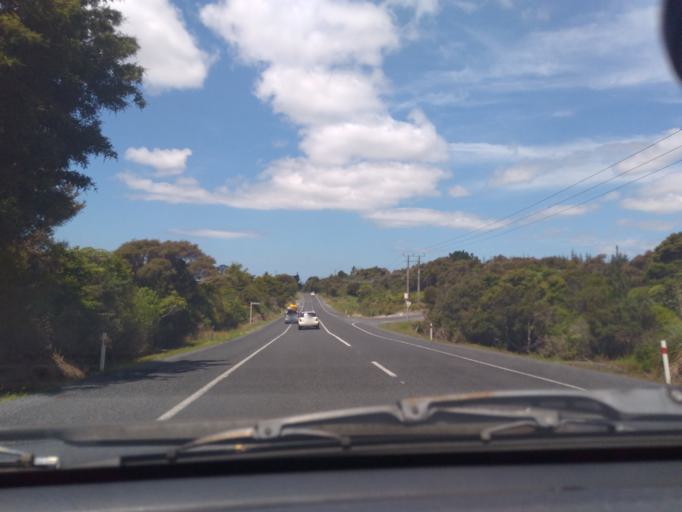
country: NZ
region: Northland
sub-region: Far North District
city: Kerikeri
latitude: -35.1214
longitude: 173.8615
